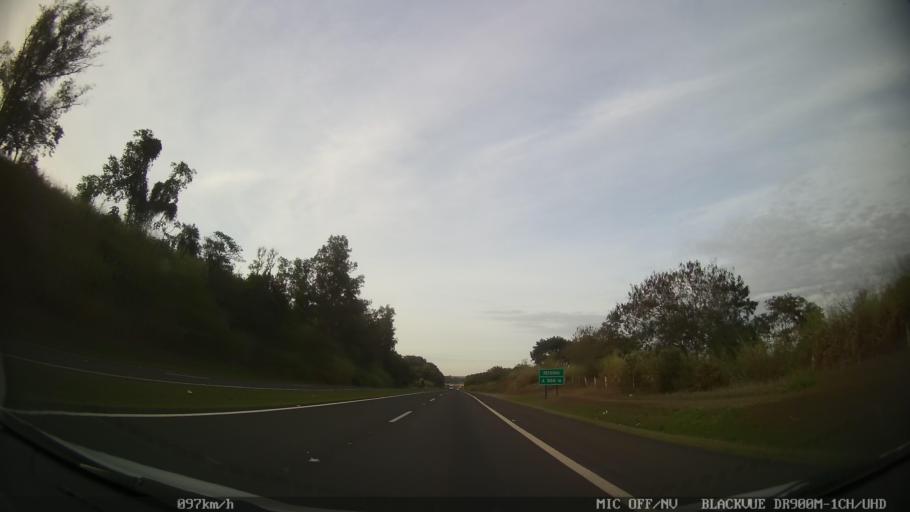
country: BR
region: Sao Paulo
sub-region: Piracicaba
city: Piracicaba
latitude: -22.6914
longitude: -47.5877
